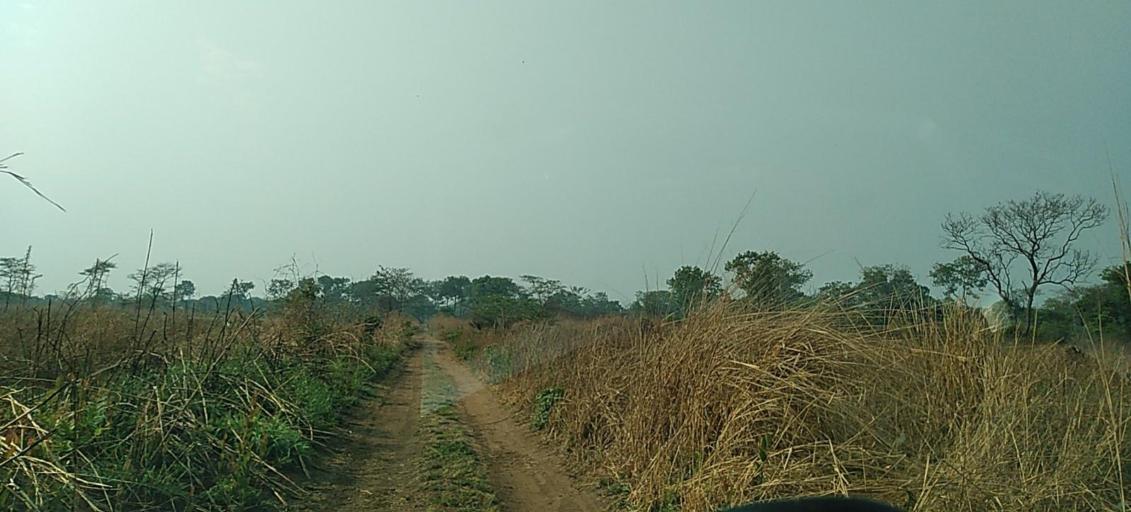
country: ZM
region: North-Western
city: Solwezi
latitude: -12.3797
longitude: 26.5643
